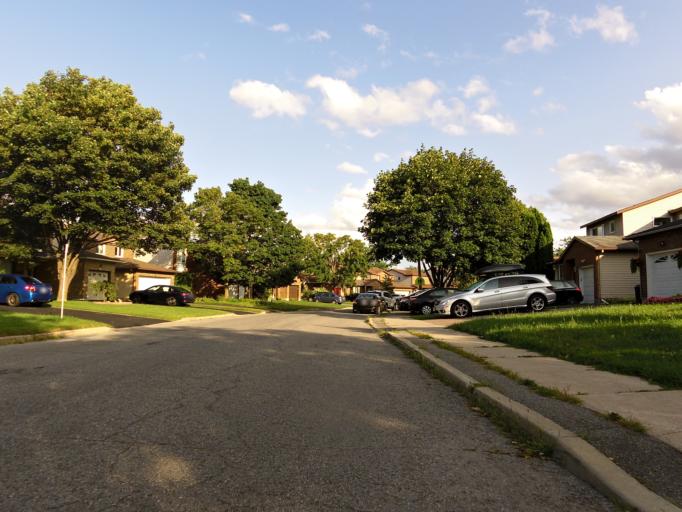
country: CA
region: Ontario
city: Ottawa
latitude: 45.3534
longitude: -75.7123
